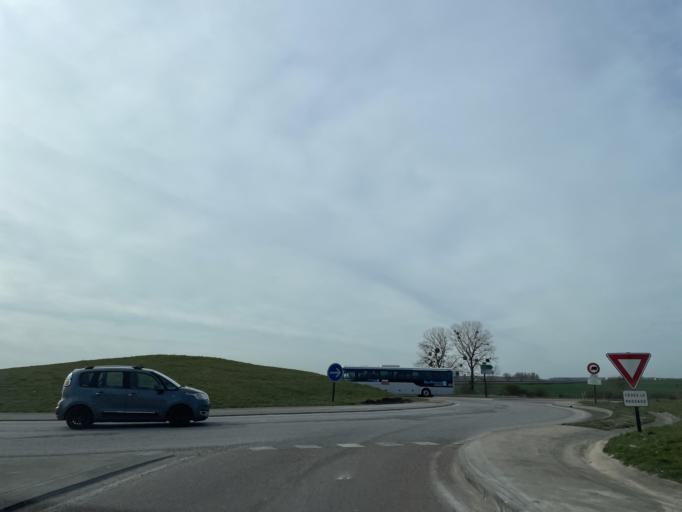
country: FR
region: Ile-de-France
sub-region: Departement de Seine-et-Marne
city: Jouy-le-Chatel
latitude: 48.6873
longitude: 3.1038
